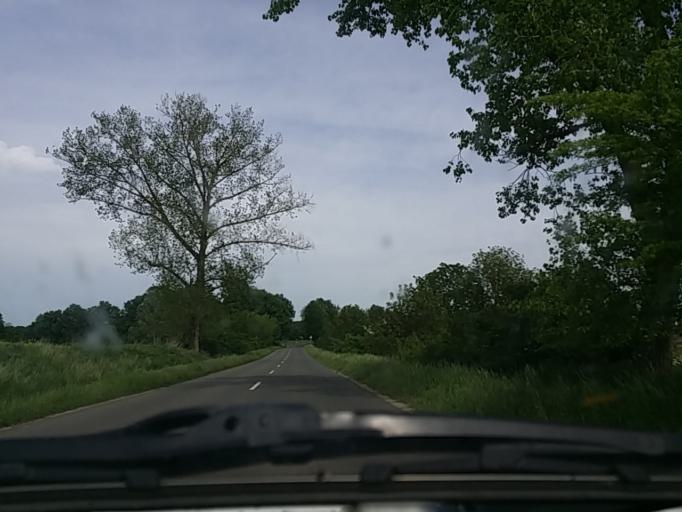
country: HU
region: Baranya
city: Vajszlo
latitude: 45.8412
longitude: 18.0607
